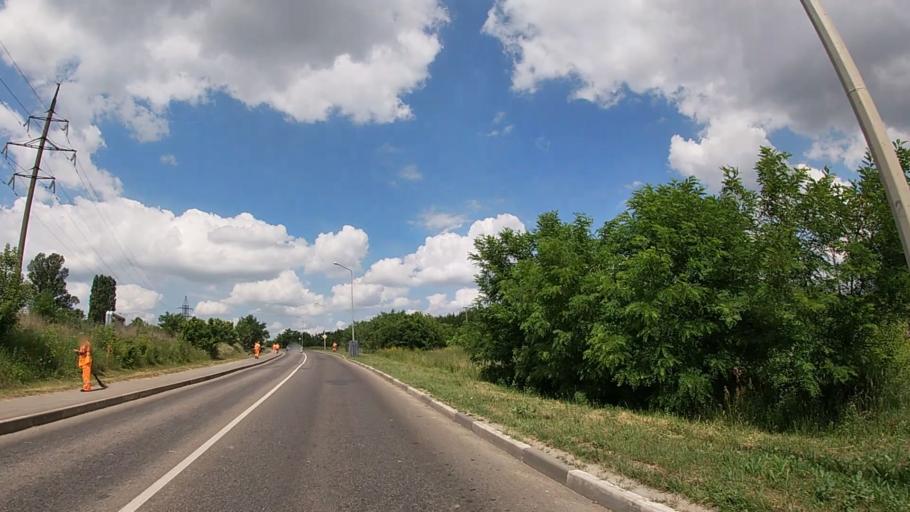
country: RU
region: Belgorod
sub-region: Belgorodskiy Rayon
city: Belgorod
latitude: 50.5931
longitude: 36.5602
